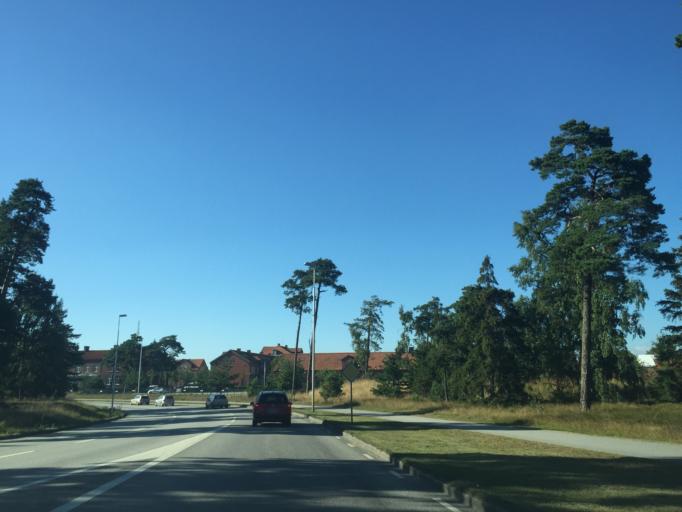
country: SE
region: Skane
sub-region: Ystads Kommun
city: Ystad
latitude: 55.4303
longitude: 13.8431
